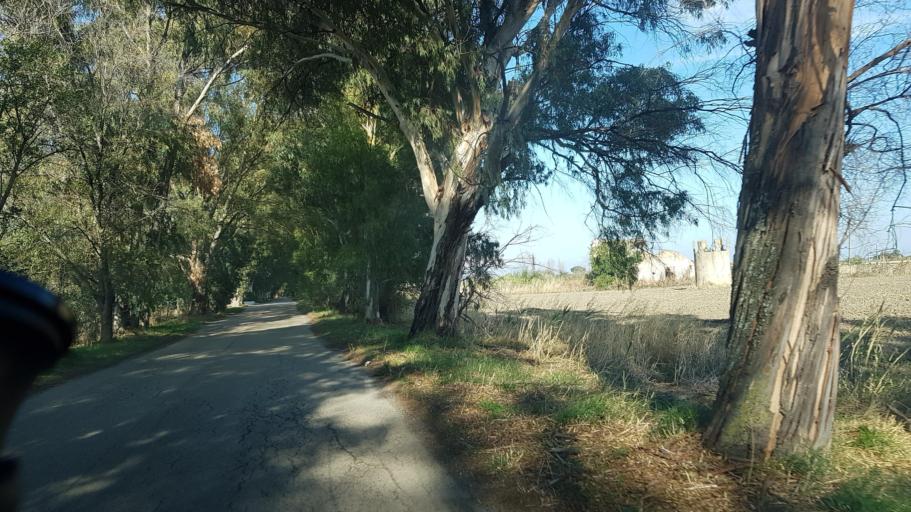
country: IT
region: Apulia
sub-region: Provincia di Foggia
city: Carapelle
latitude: 41.3920
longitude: 15.6512
